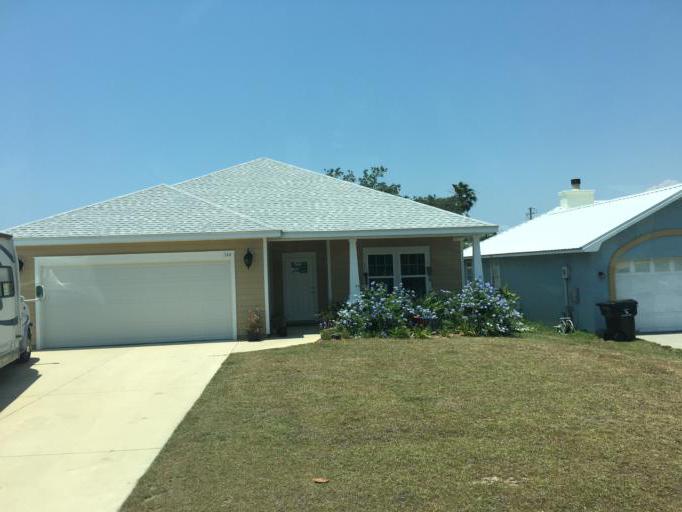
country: US
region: Florida
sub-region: Bay County
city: Panama City Beach
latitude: 30.2067
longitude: -85.8508
